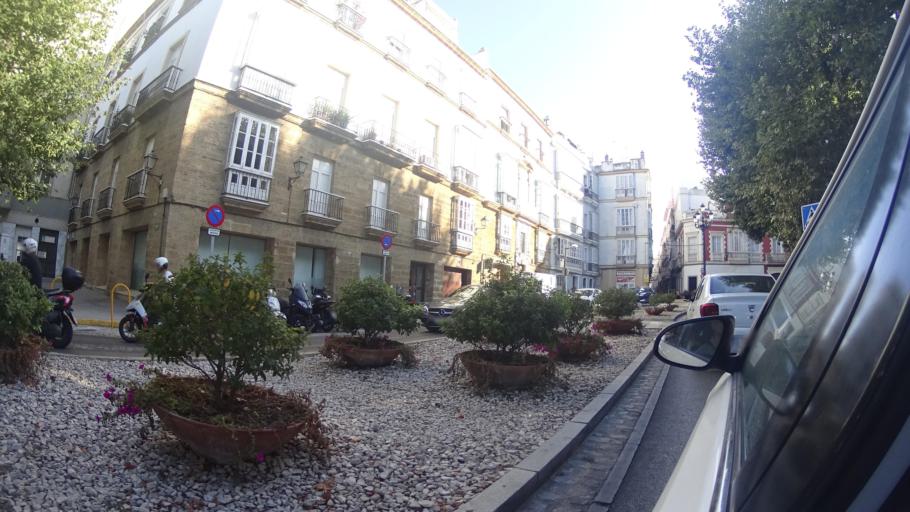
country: ES
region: Andalusia
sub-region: Provincia de Cadiz
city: Cadiz
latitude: 36.5366
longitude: -6.2969
